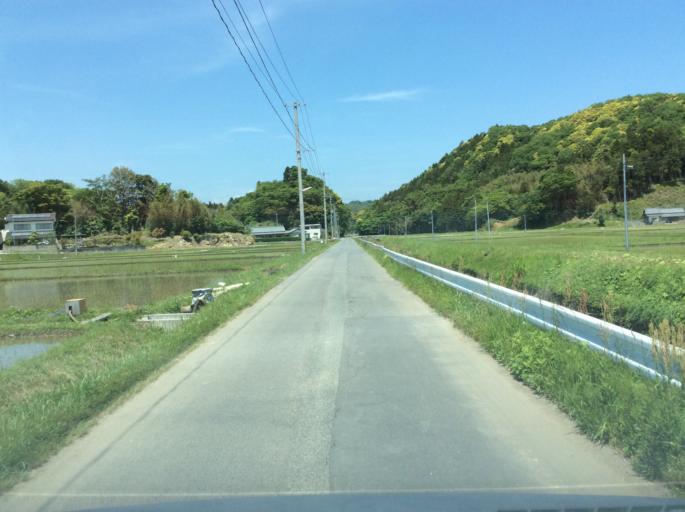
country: JP
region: Fukushima
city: Iwaki
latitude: 37.0186
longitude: 140.9392
